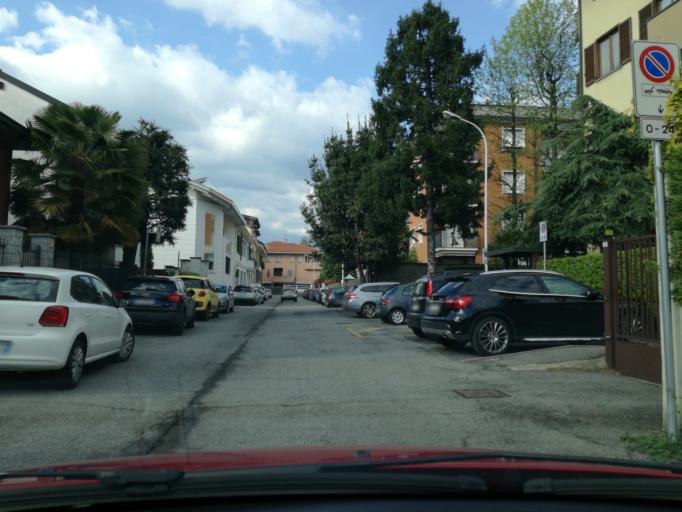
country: IT
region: Lombardy
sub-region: Provincia di Monza e Brianza
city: Seregno
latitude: 45.6549
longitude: 9.2077
